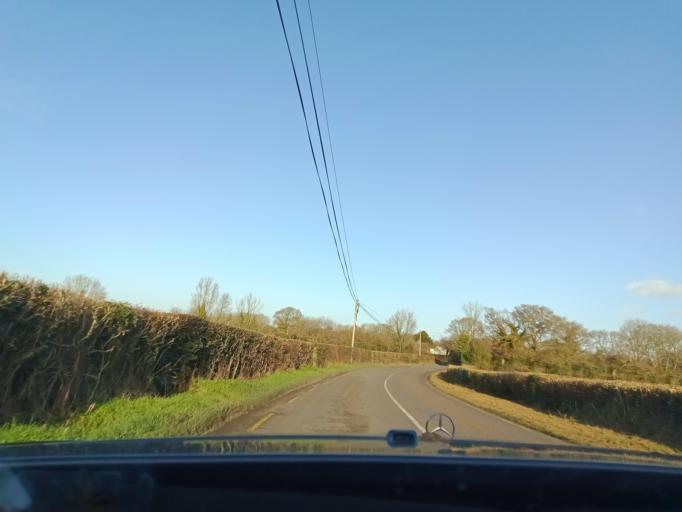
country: IE
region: Leinster
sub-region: Kilkenny
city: Callan
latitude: 52.5166
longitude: -7.3859
